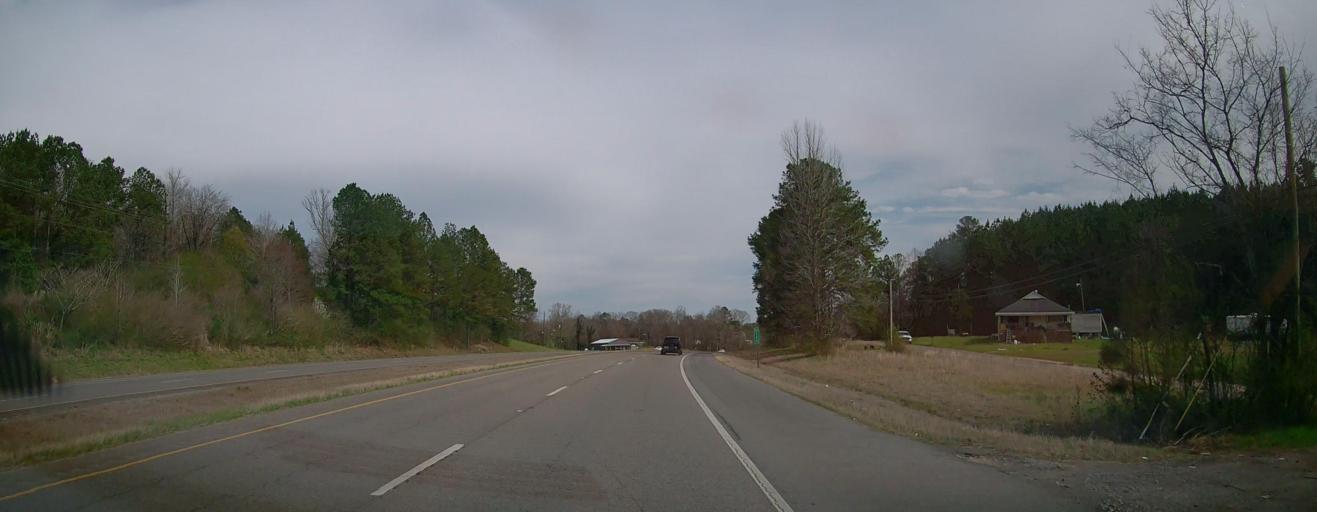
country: US
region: Alabama
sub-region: Walker County
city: Sumiton
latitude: 33.7930
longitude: -87.0951
